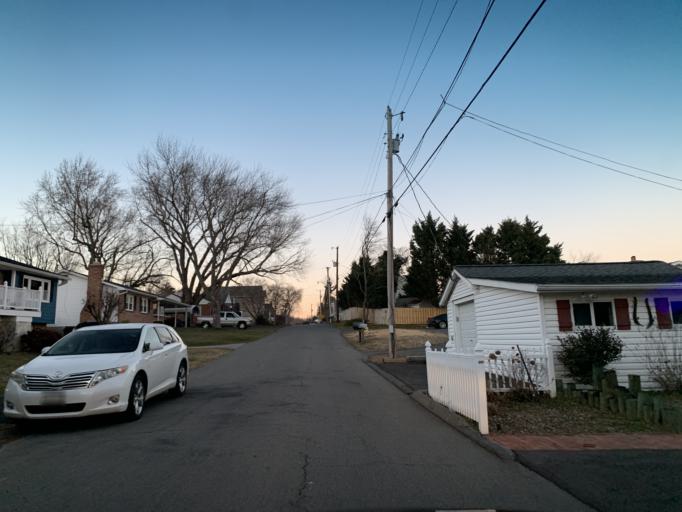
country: US
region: Maryland
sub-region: Calvert County
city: Prince Frederick
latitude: 38.5609
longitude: -76.5162
